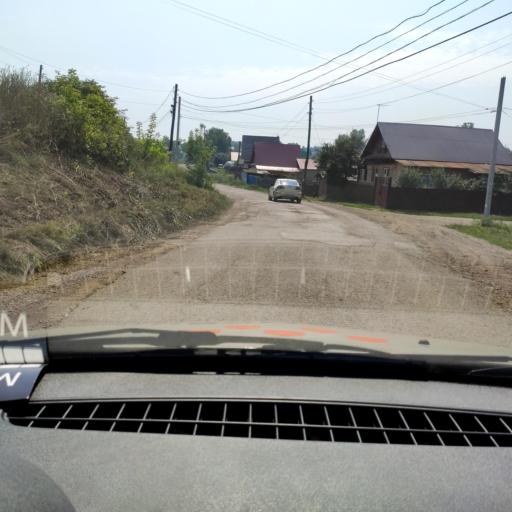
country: RU
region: Bashkortostan
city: Iglino
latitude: 54.8400
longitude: 56.4115
